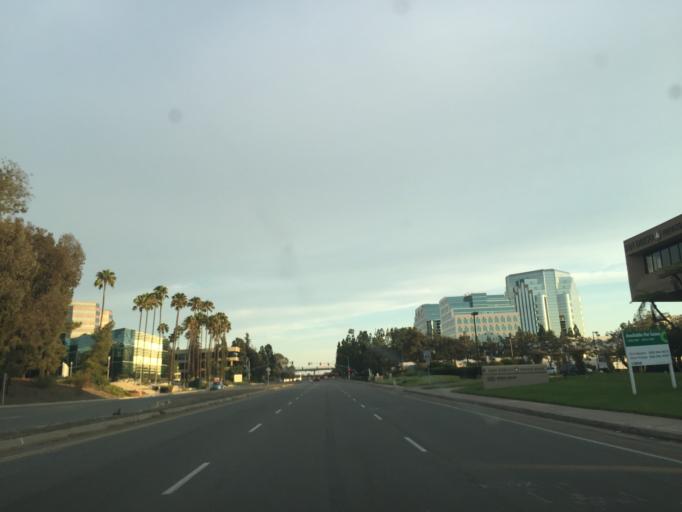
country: US
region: California
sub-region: San Diego County
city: La Jolla
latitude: 32.8774
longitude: -117.2142
